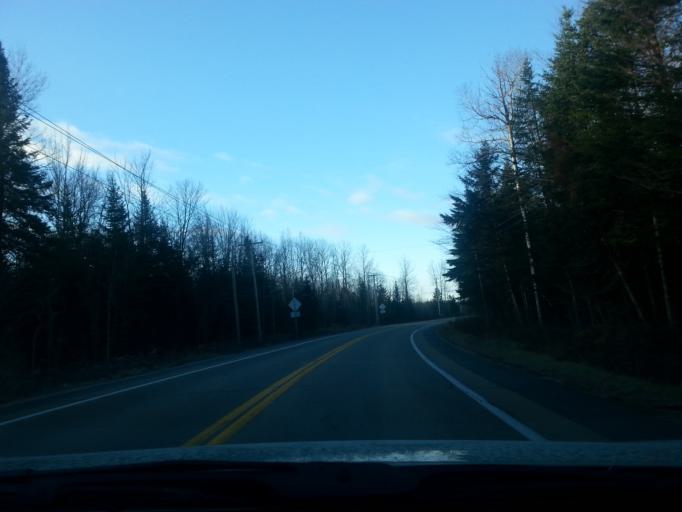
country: CA
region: Quebec
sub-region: Capitale-Nationale
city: Saint-Marc-des-Carrieres
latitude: 46.6736
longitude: -72.0800
